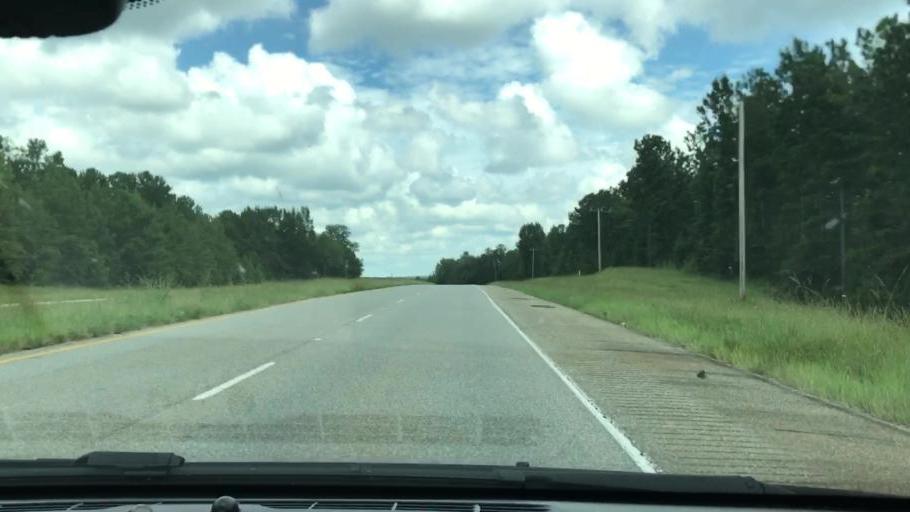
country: US
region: Georgia
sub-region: Stewart County
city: Lumpkin
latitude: 32.1416
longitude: -84.8265
